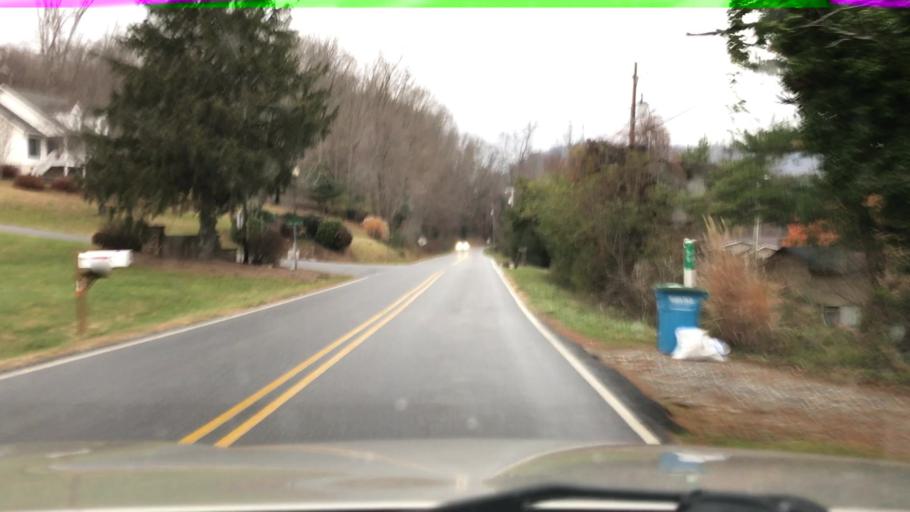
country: US
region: North Carolina
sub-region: Buncombe County
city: Avery Creek
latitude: 35.4749
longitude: -82.5580
